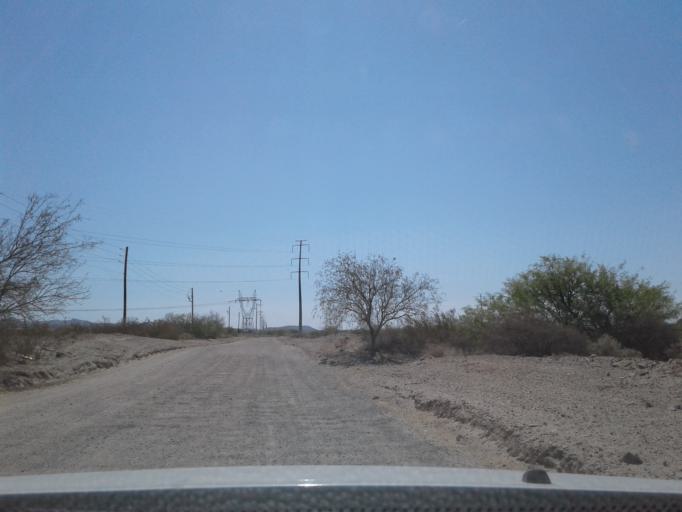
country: US
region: Arizona
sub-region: Maricopa County
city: Laveen
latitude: 33.2904
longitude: -112.1389
